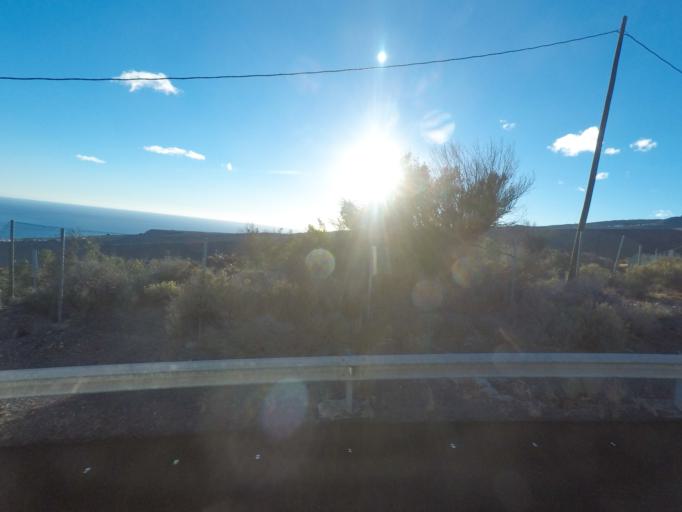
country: ES
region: Canary Islands
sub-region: Provincia de Santa Cruz de Tenerife
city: Alajero
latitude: 28.0450
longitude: -17.1977
